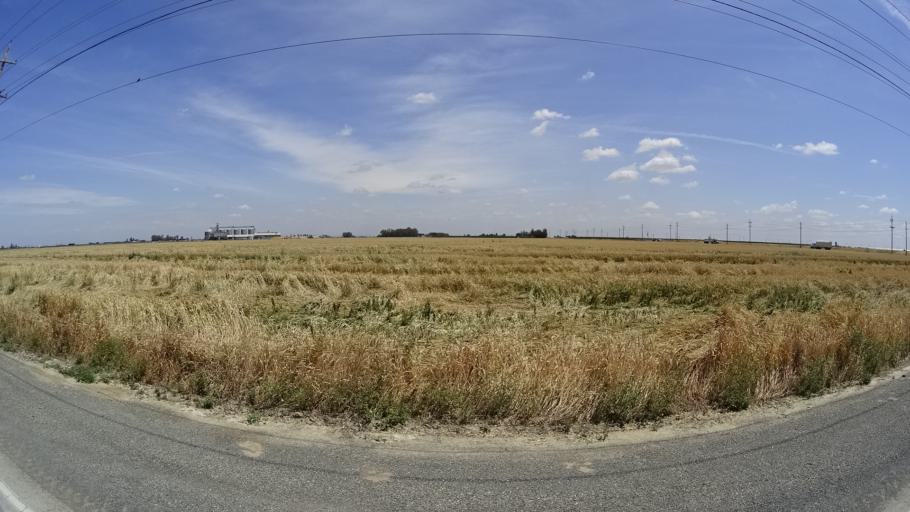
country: US
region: California
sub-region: Kings County
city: Home Garden
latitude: 36.2126
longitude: -119.6549
